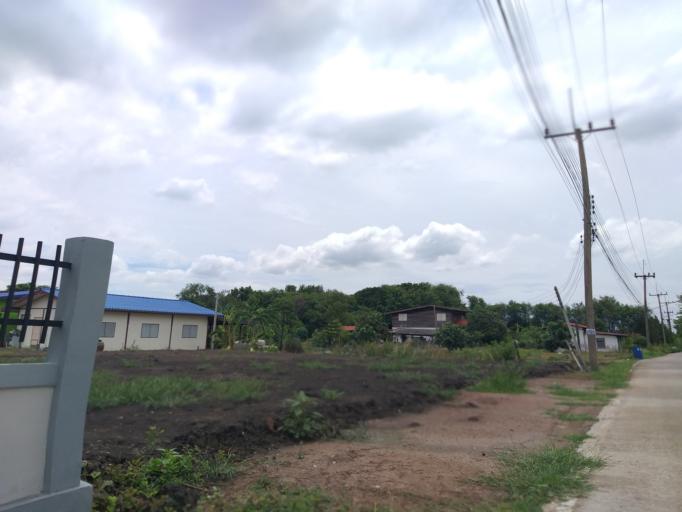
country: TH
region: Pathum Thani
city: Ban Lam Luk Ka
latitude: 13.9685
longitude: 100.8540
